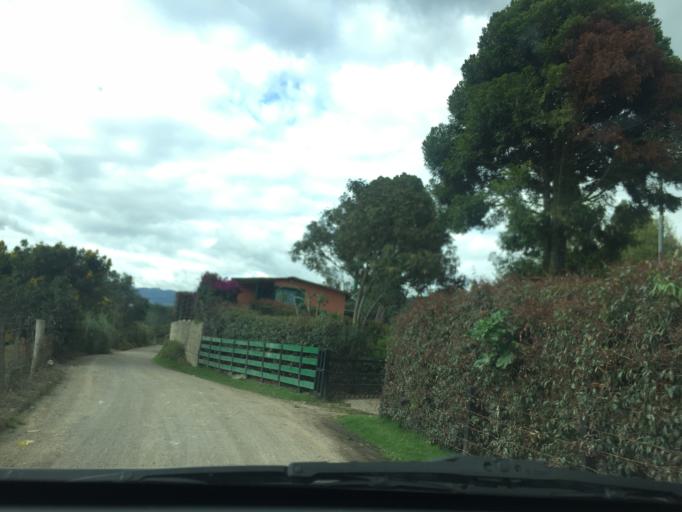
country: CO
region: Cundinamarca
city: Subachoque
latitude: 4.9384
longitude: -74.1473
